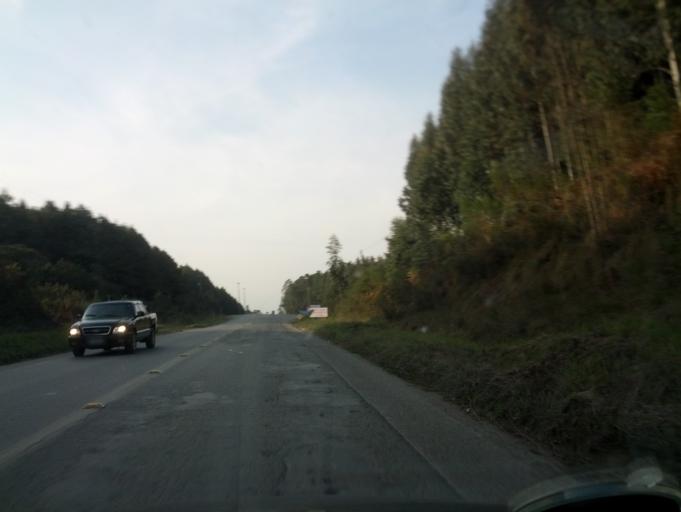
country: BR
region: Santa Catarina
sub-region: Otacilio Costa
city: Otacilio Costa
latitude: -27.5138
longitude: -50.1318
